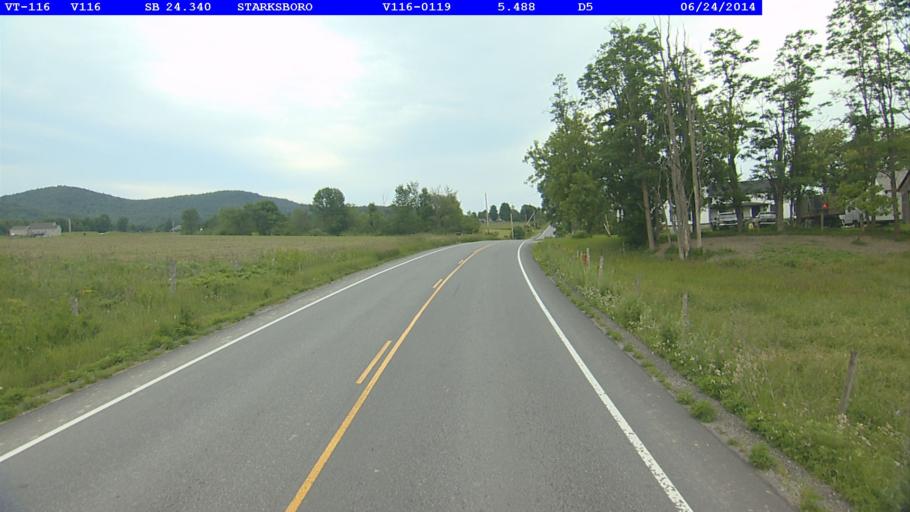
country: US
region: Vermont
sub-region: Chittenden County
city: Hinesburg
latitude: 44.2632
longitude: -73.0653
